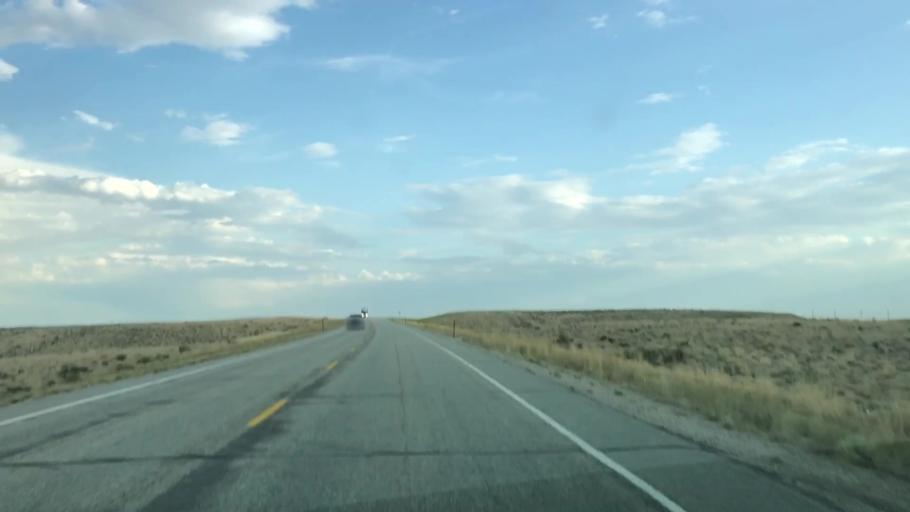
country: US
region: Wyoming
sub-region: Sweetwater County
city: North Rock Springs
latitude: 42.2796
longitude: -109.4850
